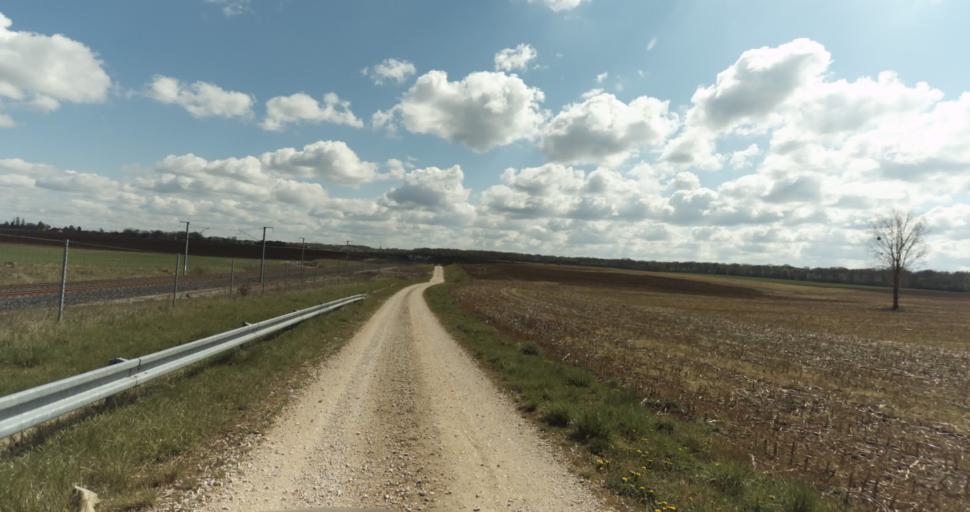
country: FR
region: Bourgogne
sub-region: Departement de la Cote-d'Or
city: Auxonne
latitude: 47.2223
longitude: 5.4314
